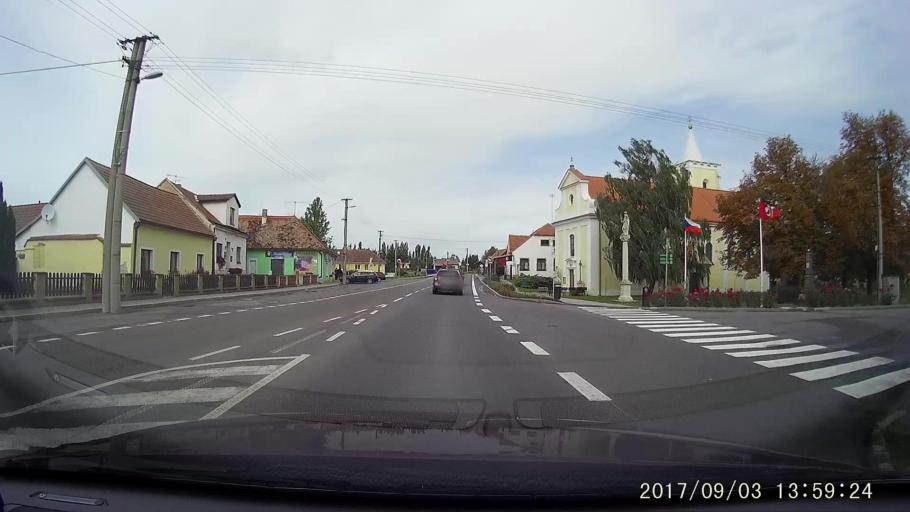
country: CZ
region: South Moravian
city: Vrbovec
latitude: 48.7865
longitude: 16.0823
